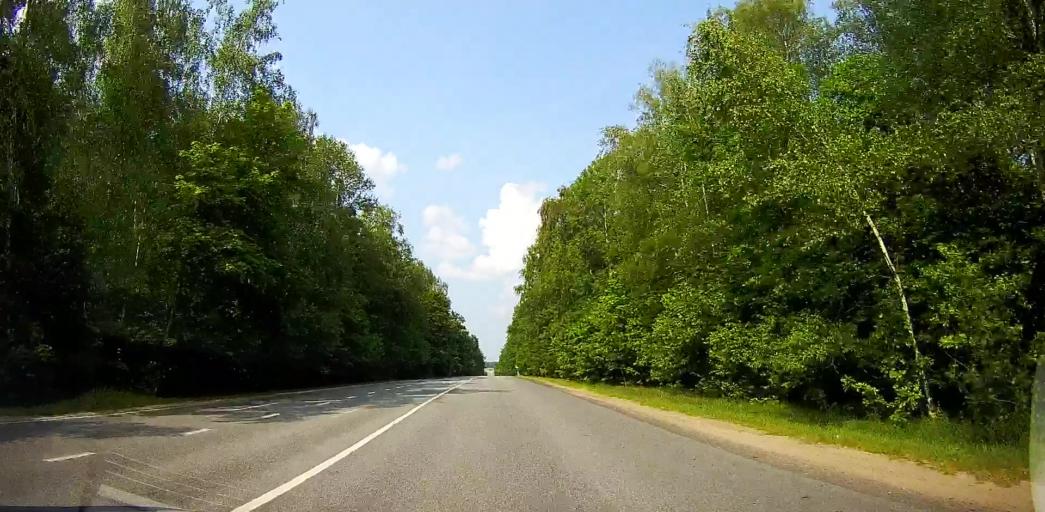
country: RU
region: Moskovskaya
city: Malino
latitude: 55.0097
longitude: 38.1721
